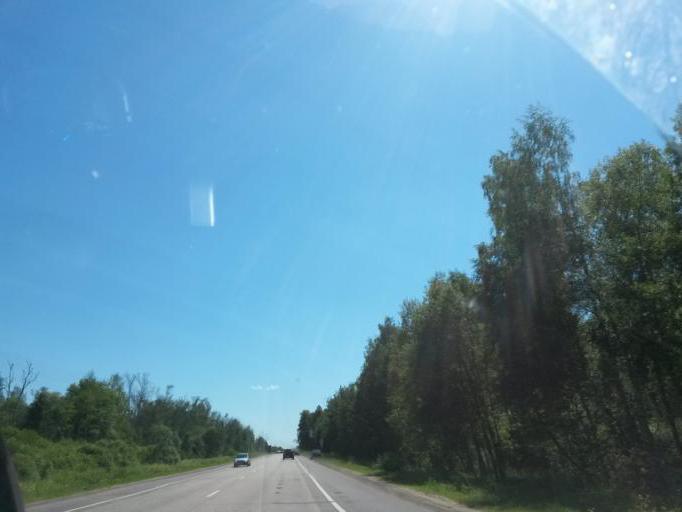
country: RU
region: Moskovskaya
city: Proletarskiy
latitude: 55.0489
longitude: 37.4323
